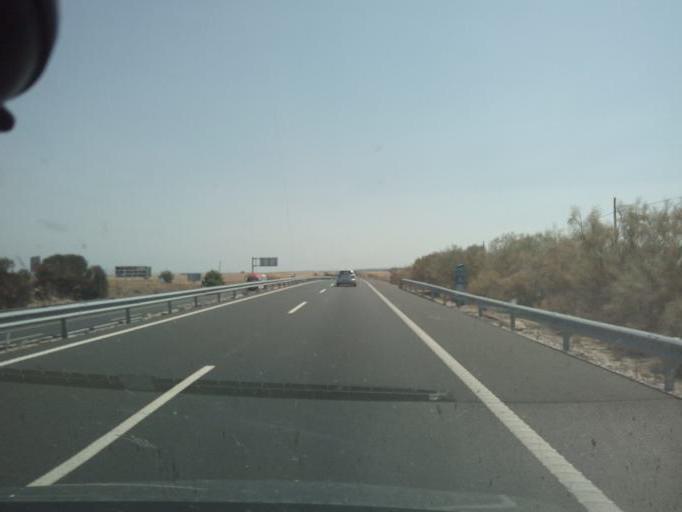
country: ES
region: Extremadura
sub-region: Provincia de Caceres
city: Peraleda de la Mata
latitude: 39.8909
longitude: -5.4211
